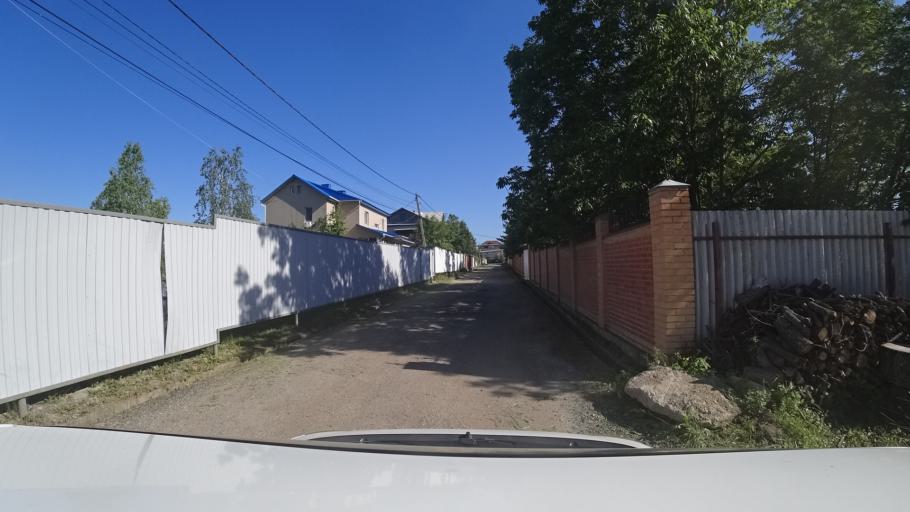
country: RU
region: Khabarovsk Krai
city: Topolevo
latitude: 48.5430
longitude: 135.1776
